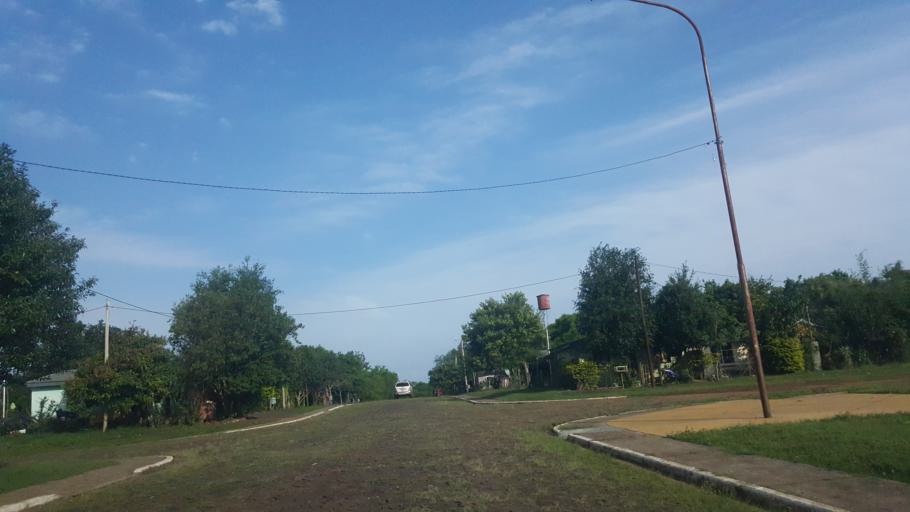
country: AR
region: Misiones
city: Cerro Cora
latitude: -27.5615
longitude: -55.7040
